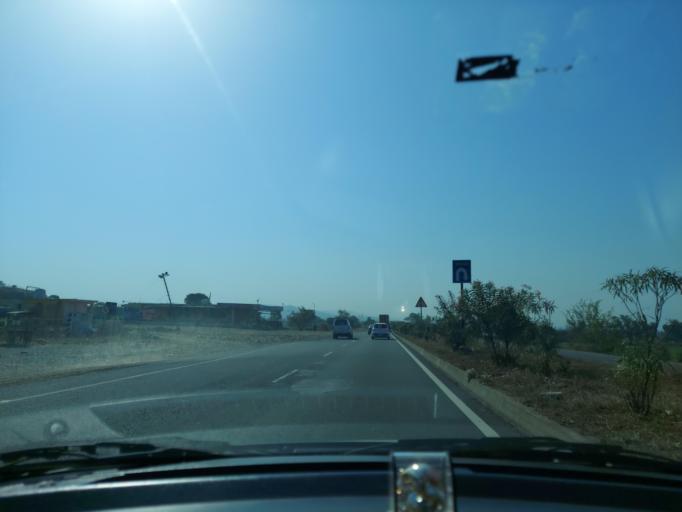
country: IN
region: Madhya Pradesh
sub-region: Indore
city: Pithampur
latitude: 22.5648
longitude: 75.6489
